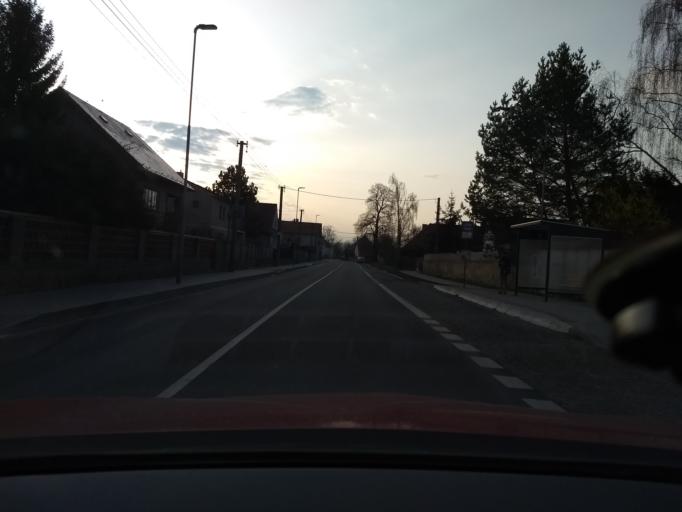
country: CZ
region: Central Bohemia
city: Jenec
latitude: 50.0518
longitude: 14.1755
